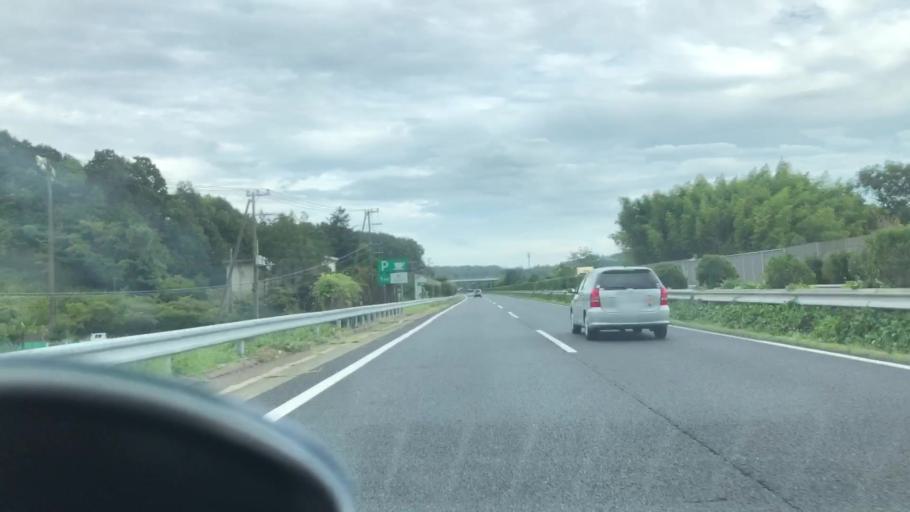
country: JP
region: Hyogo
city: Yashiro
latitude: 34.9245
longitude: 134.9889
